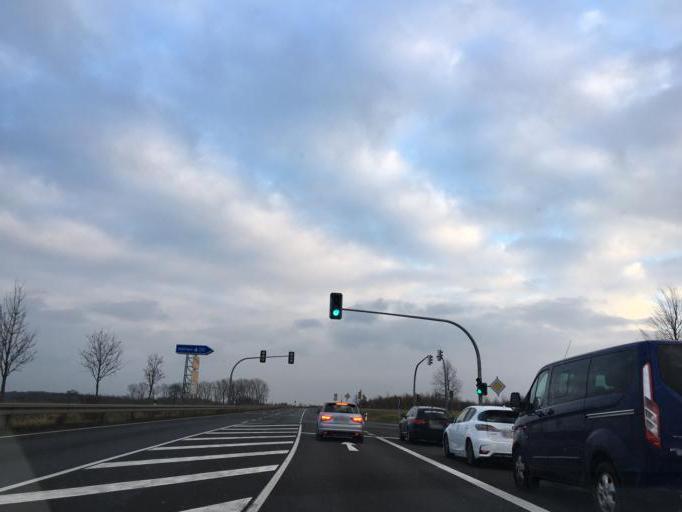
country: DE
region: Saxony
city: Grossposna
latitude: 51.2643
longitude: 12.4631
